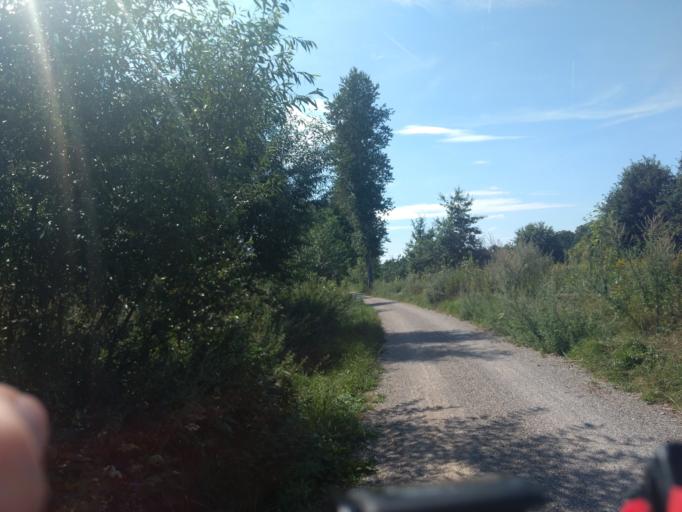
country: DE
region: North Rhine-Westphalia
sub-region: Regierungsbezirk Detmold
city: Delbruck
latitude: 51.7652
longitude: 8.6112
